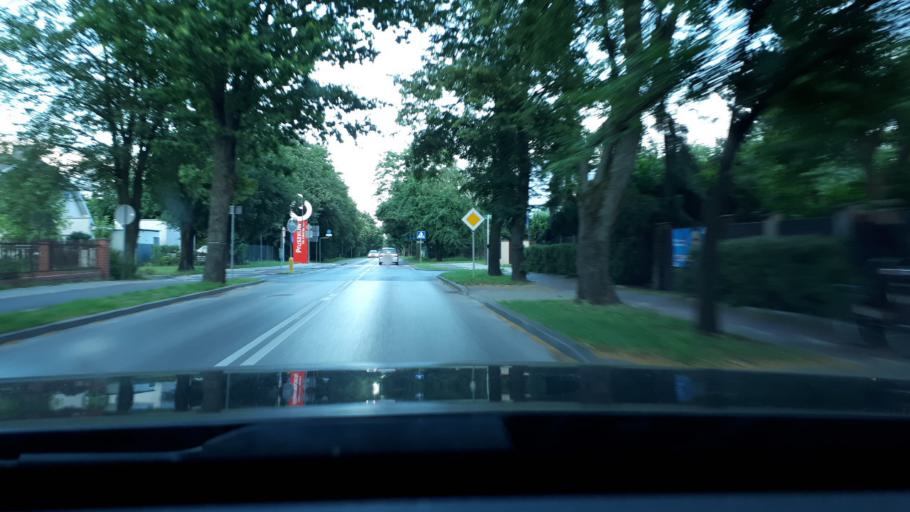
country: PL
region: Masovian Voivodeship
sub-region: Powiat pruszkowski
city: Komorow
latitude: 52.1582
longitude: 20.8233
